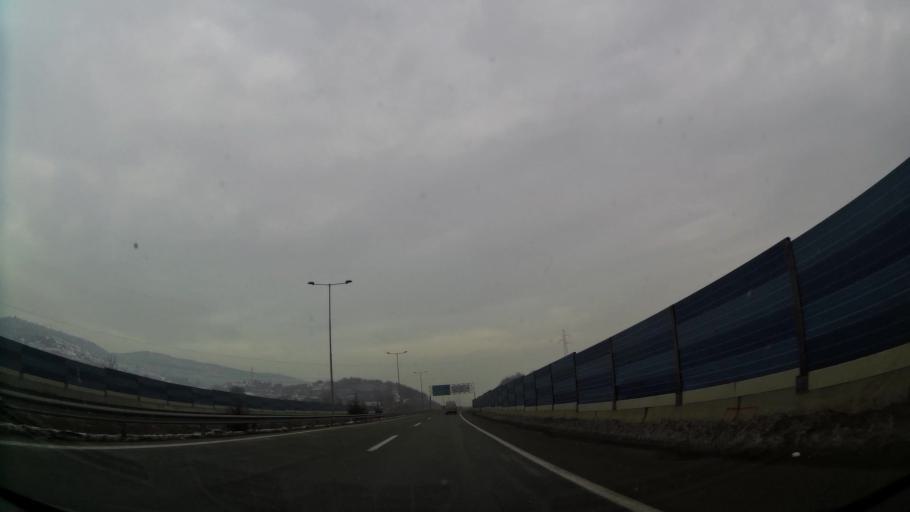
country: MK
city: Kondovo
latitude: 42.0329
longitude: 21.3319
